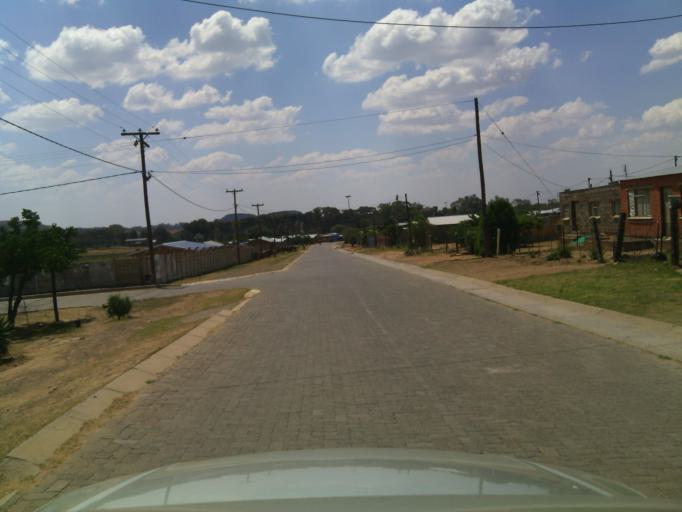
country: ZA
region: Orange Free State
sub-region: Xhariep District Municipality
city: Dewetsdorp
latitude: -29.5824
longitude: 26.6794
